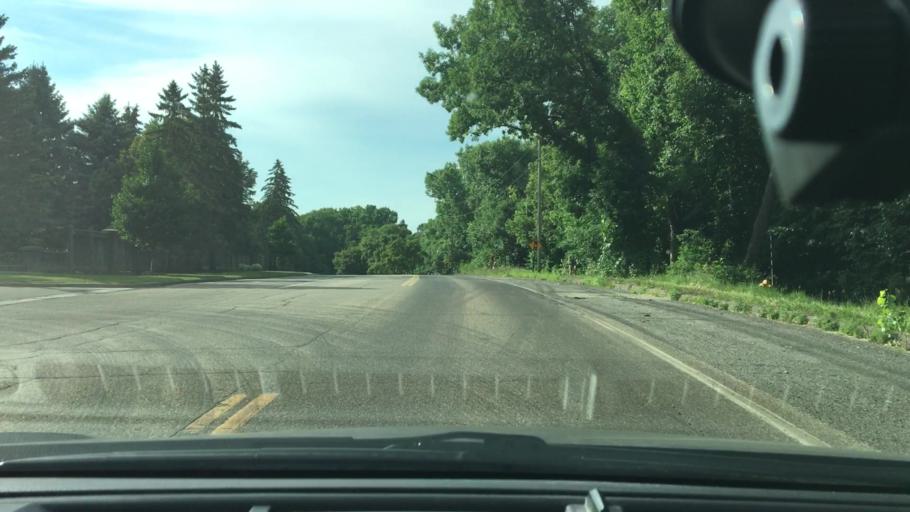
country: US
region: Minnesota
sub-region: Hennepin County
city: Plymouth
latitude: 45.0159
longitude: -93.4402
